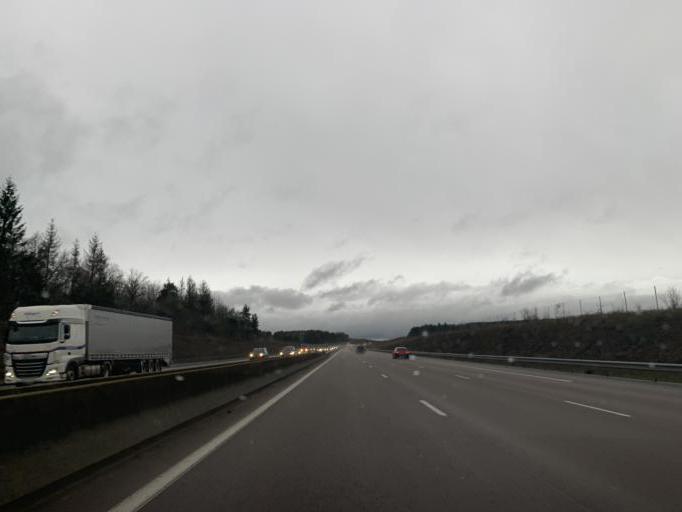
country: FR
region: Champagne-Ardenne
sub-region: Departement de la Haute-Marne
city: Rolampont
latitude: 47.8629
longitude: 5.2235
